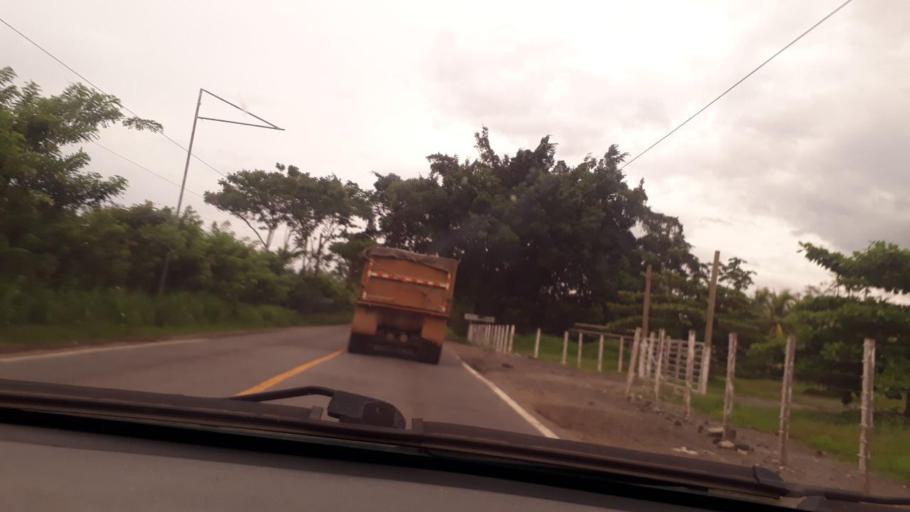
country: GT
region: Izabal
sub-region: Municipio de Los Amates
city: Los Amates
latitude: 15.2994
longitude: -89.0645
